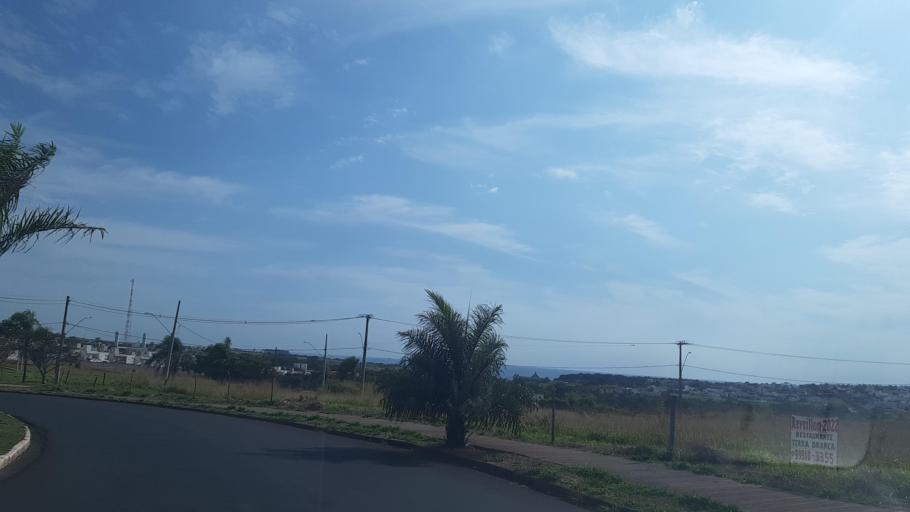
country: BR
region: Minas Gerais
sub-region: Uberlandia
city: Uberlandia
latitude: -18.8824
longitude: -48.2422
